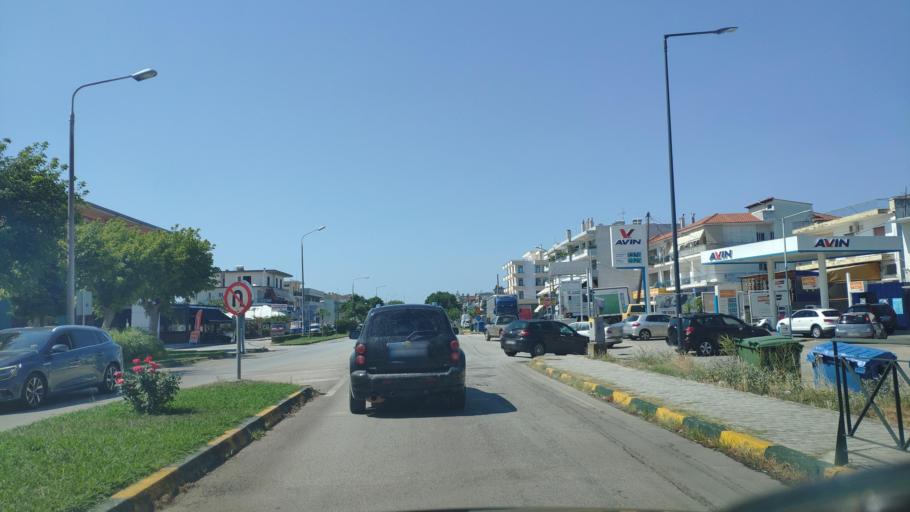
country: GR
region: Epirus
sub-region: Nomos Artas
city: Arta
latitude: 39.1606
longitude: 20.9805
